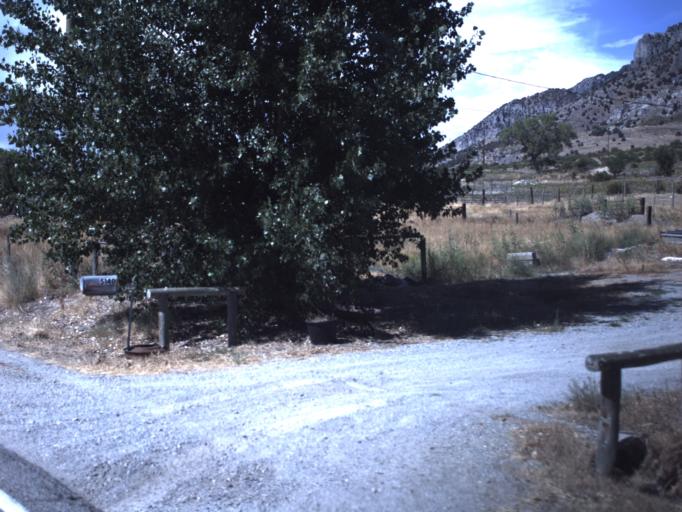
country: US
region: Utah
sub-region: Box Elder County
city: Honeyville
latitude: 41.6018
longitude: -112.0523
